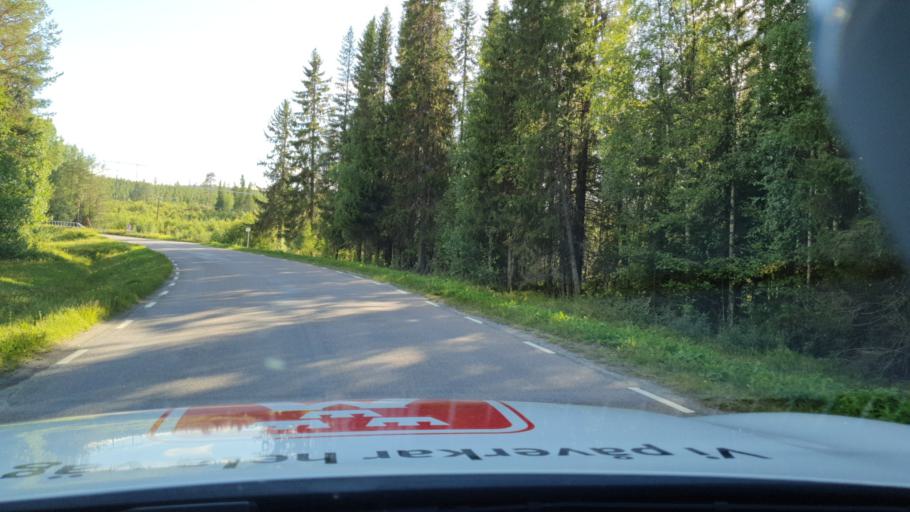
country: SE
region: Jaemtland
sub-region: Stroemsunds Kommun
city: Stroemsund
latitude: 64.4302
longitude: 15.5508
